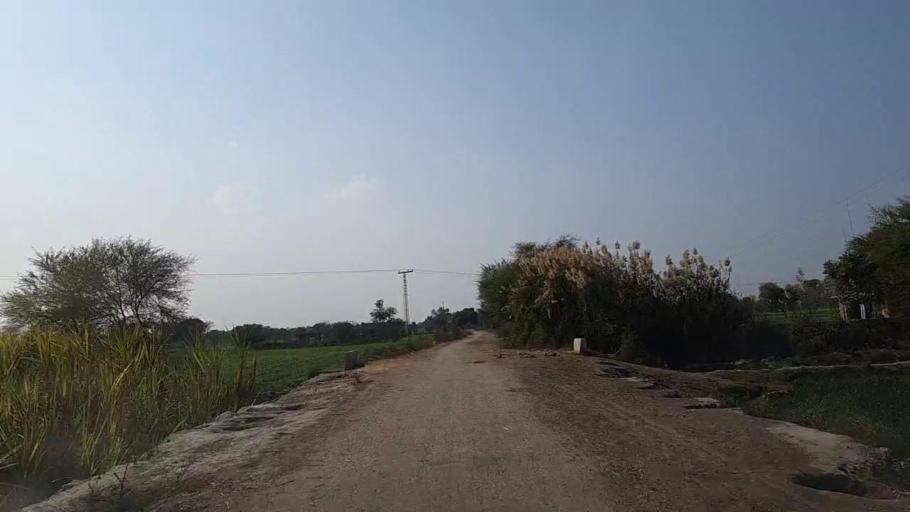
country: PK
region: Sindh
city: Jam Sahib
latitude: 26.2899
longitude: 68.5622
